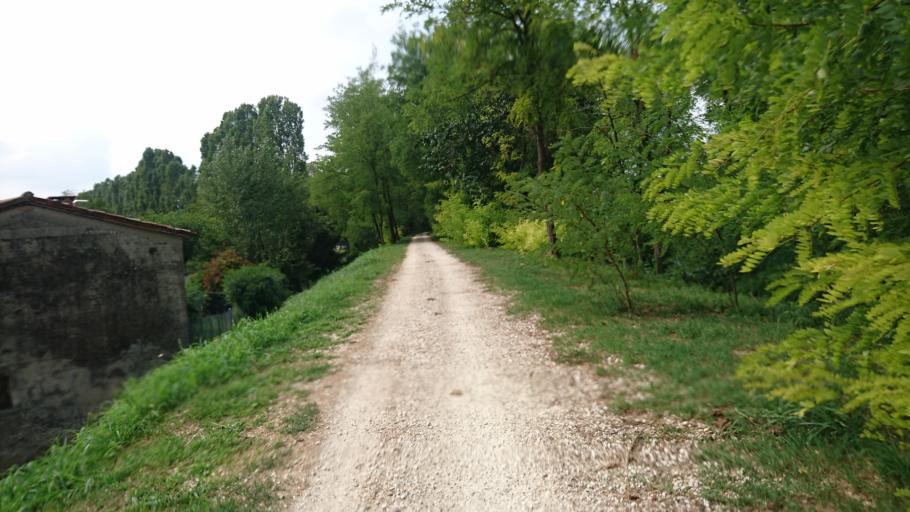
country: IT
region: Veneto
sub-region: Provincia di Padova
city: Limena
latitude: 45.4707
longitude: 11.8528
